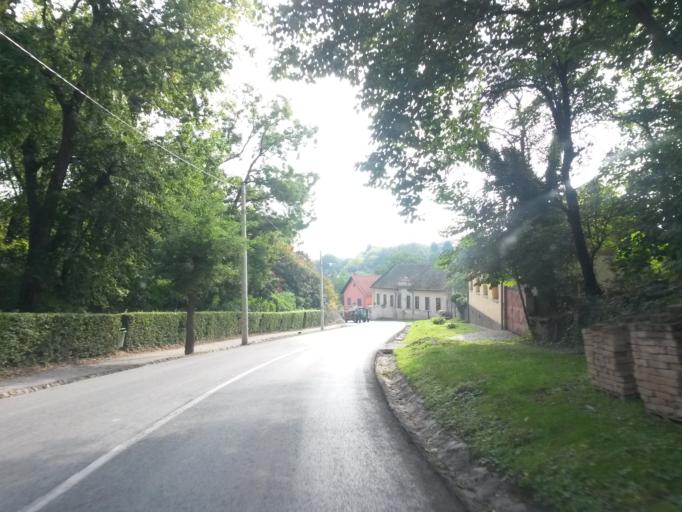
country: HR
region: Vukovarsko-Srijemska
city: Ilok
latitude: 45.2231
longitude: 19.3719
